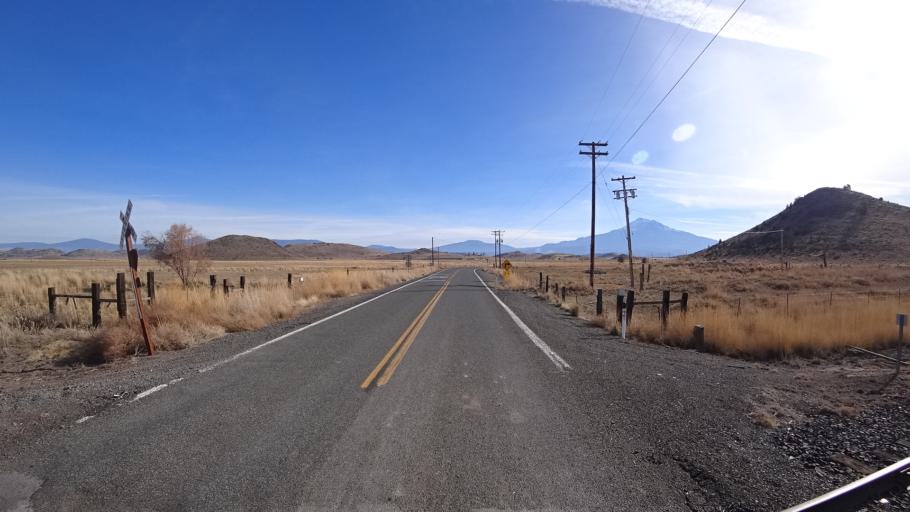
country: US
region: California
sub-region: Siskiyou County
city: Weed
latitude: 41.5381
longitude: -122.5248
